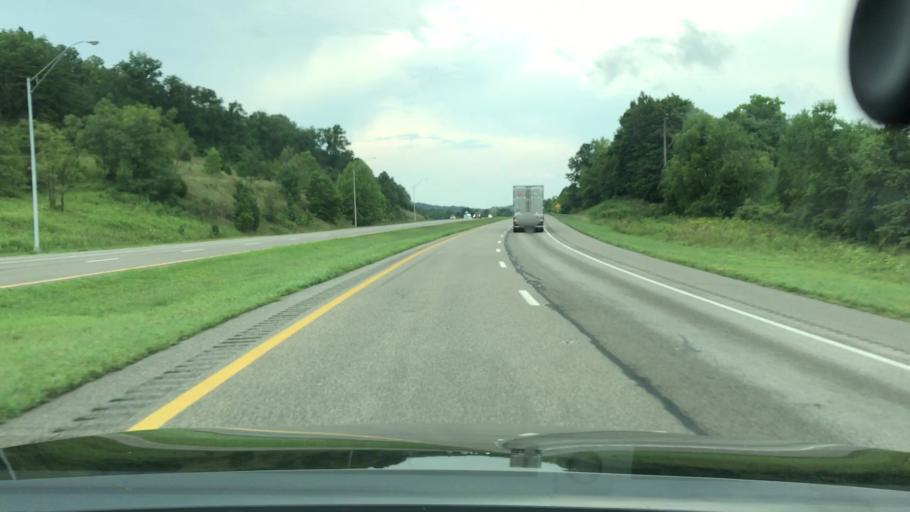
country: US
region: Ohio
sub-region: Gallia County
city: Gallipolis
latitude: 38.8480
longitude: -82.2328
